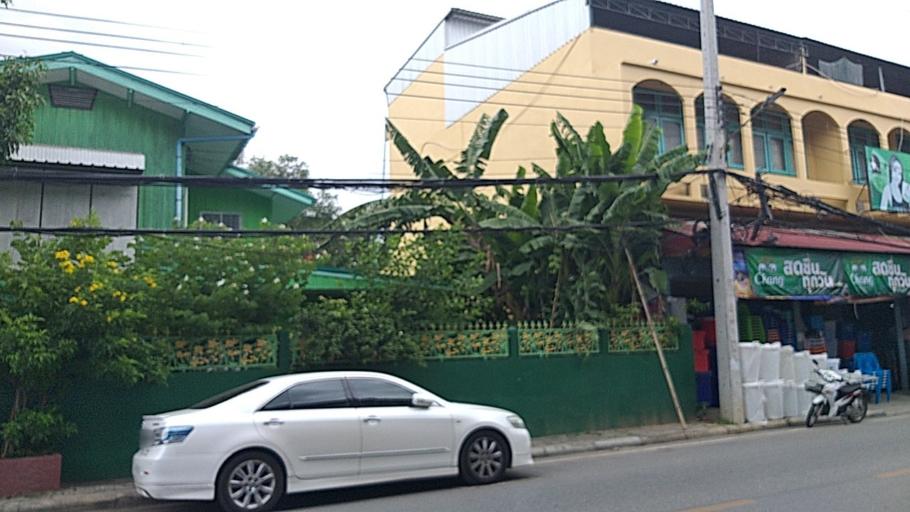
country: TH
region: Nakhon Pathom
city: Nakhon Pathom
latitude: 13.8214
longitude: 100.0502
